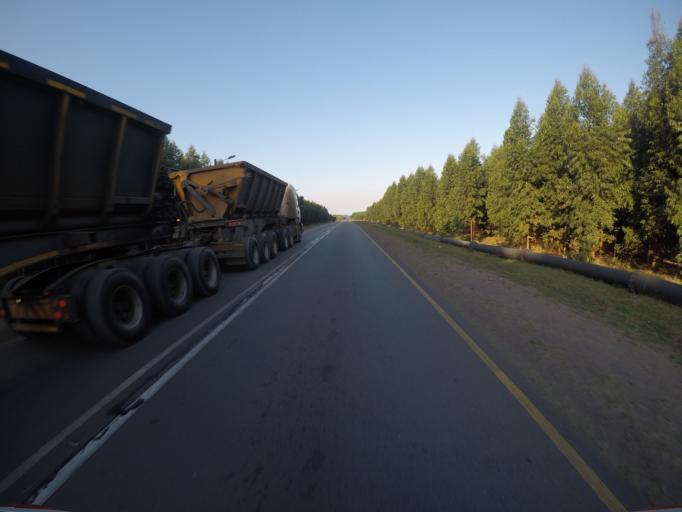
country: ZA
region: KwaZulu-Natal
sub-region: uThungulu District Municipality
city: KwaMbonambi
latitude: -28.6833
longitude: 32.1579
